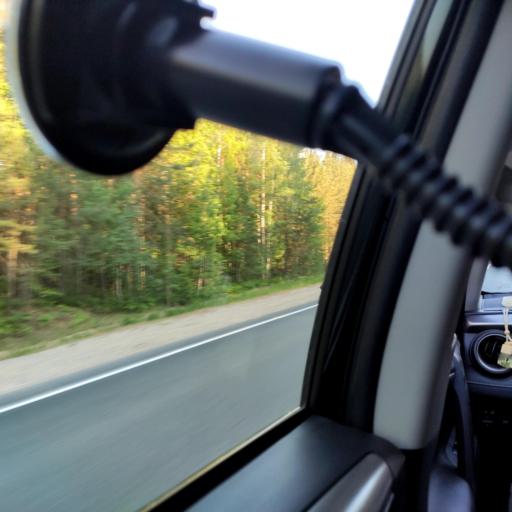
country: RU
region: Mariy-El
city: Suslonger
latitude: 56.2545
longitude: 48.2322
